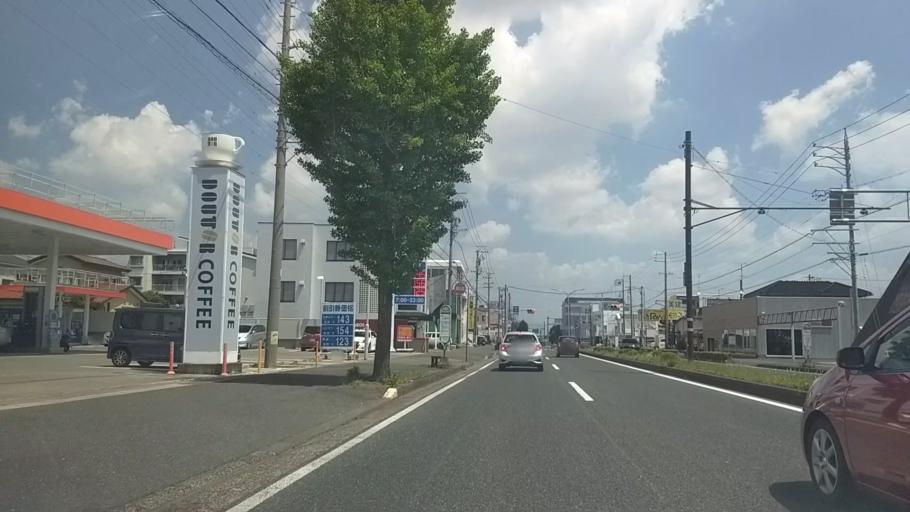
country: JP
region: Shizuoka
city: Hamamatsu
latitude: 34.7391
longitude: 137.7372
